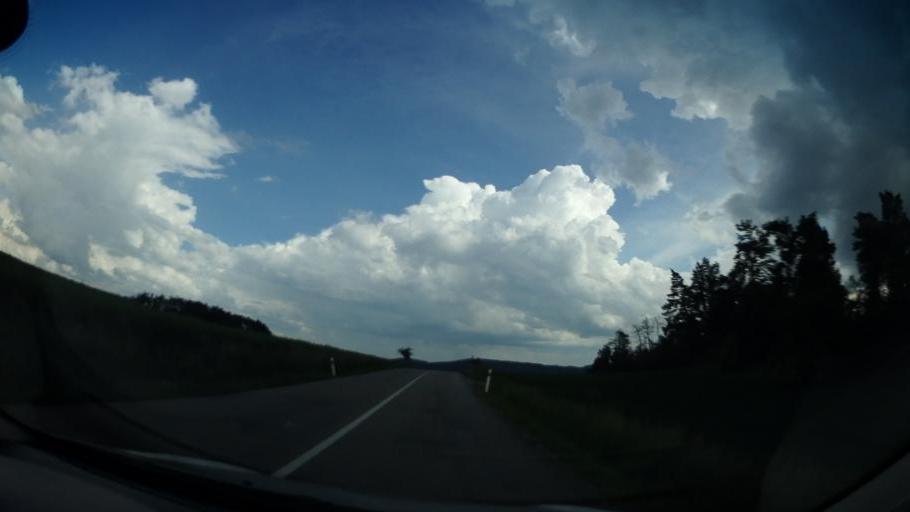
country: CZ
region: South Moravian
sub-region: Okres Brno-Venkov
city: Dolni Loucky
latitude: 49.3865
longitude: 16.3393
